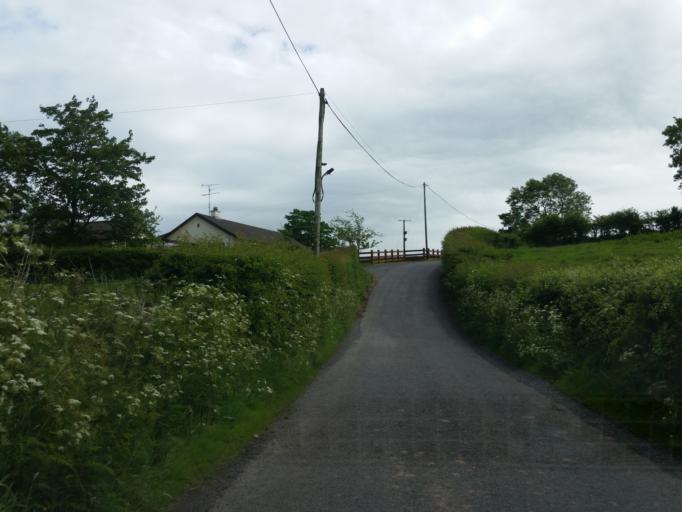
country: GB
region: Northern Ireland
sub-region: Omagh District
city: Omagh
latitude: 54.5414
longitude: -7.1457
